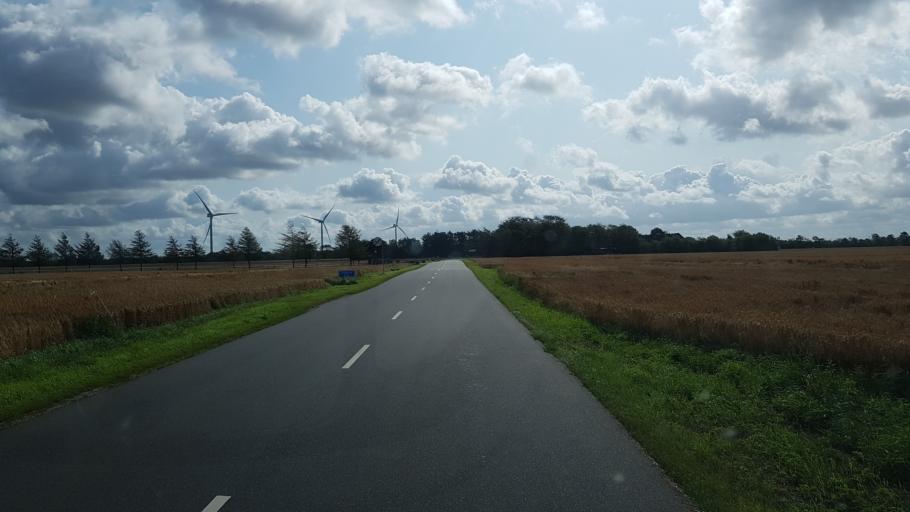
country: DK
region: South Denmark
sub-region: Billund Kommune
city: Grindsted
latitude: 55.7847
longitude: 8.8197
